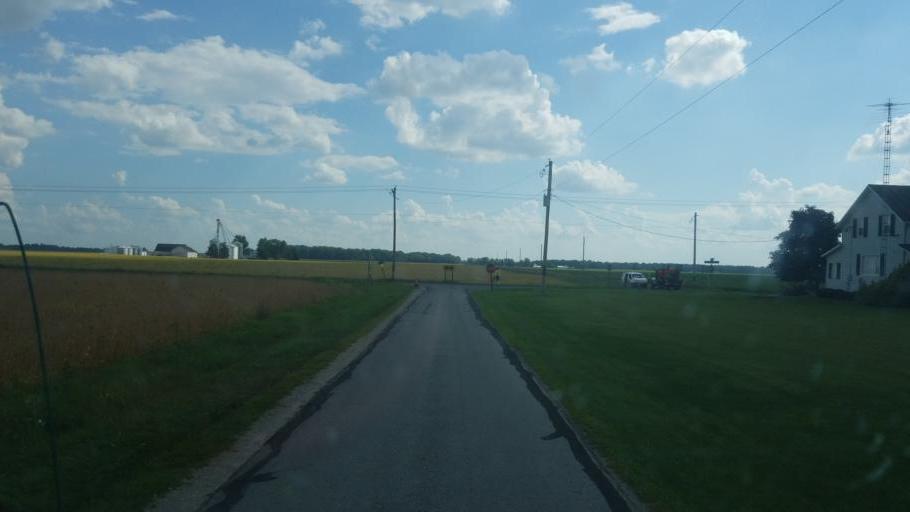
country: US
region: Ohio
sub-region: Huron County
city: Willard
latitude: 40.9943
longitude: -82.8817
